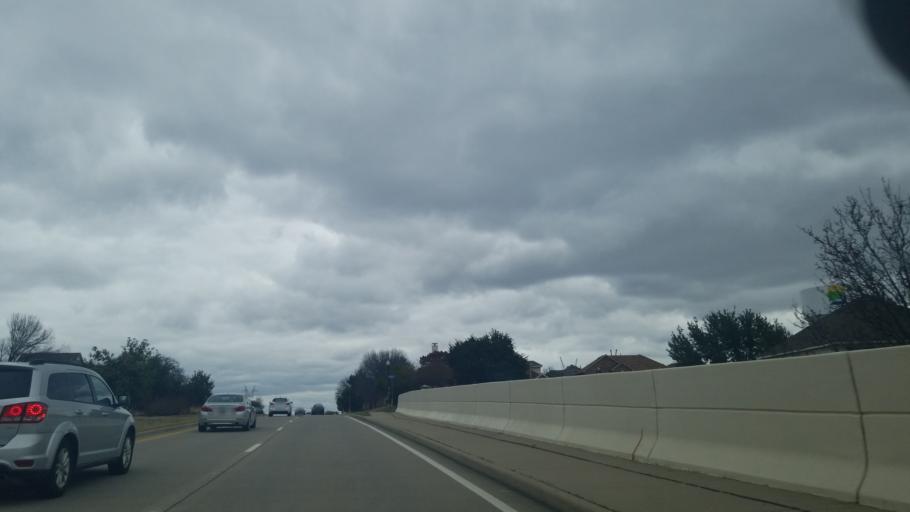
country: US
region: Texas
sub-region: Denton County
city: Copper Canyon
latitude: 33.0827
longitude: -97.0777
